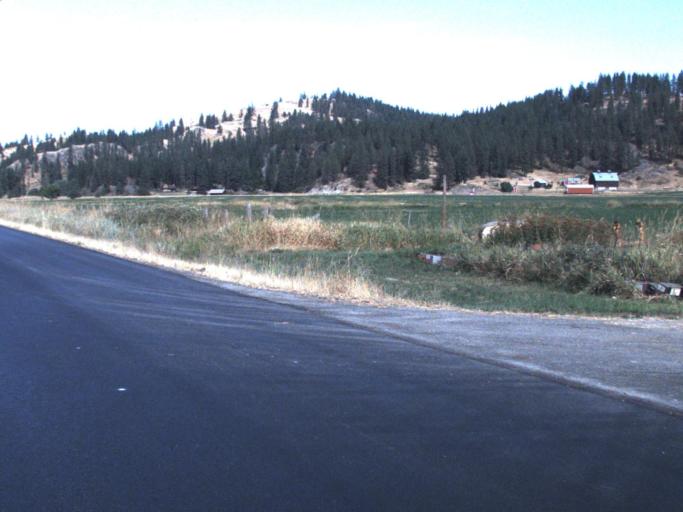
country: US
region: Washington
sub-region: Stevens County
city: Colville
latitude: 48.4696
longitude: -117.8893
